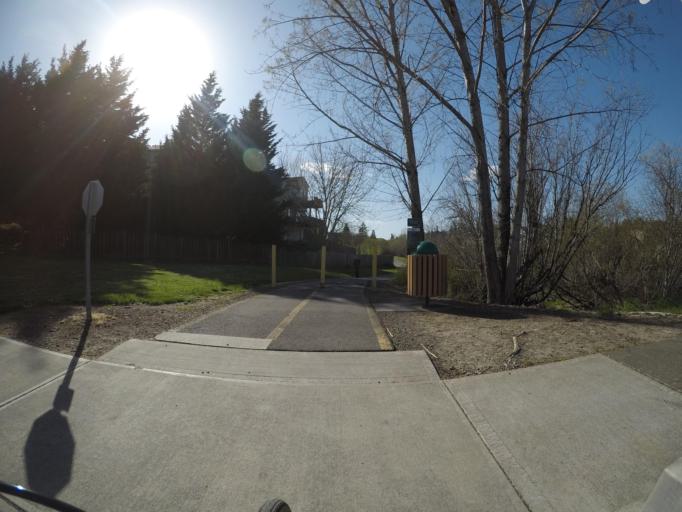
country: US
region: Oregon
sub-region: Washington County
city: Bethany
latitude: 45.5568
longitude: -122.8519
